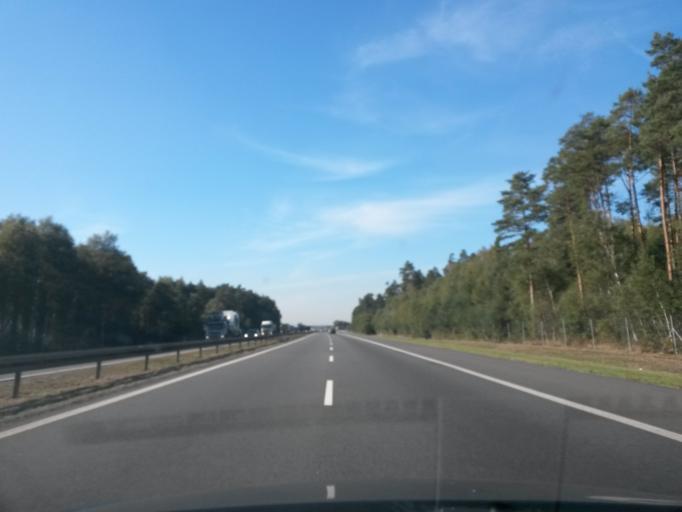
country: PL
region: Opole Voivodeship
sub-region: Powiat opolski
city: Proszkow
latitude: 50.5560
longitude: 17.8833
